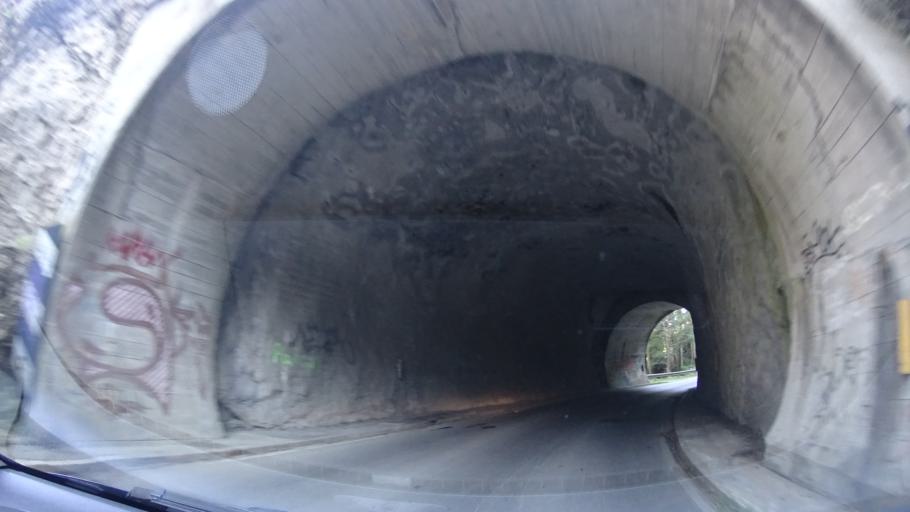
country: ES
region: Asturias
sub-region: Province of Asturias
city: Ribadesella
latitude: 43.4724
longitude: -5.1324
